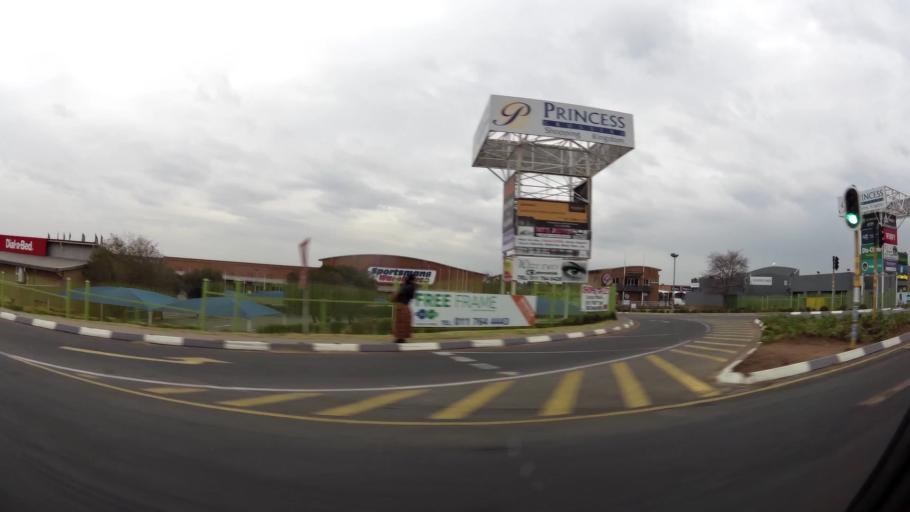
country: ZA
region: Gauteng
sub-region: City of Johannesburg Metropolitan Municipality
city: Roodepoort
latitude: -26.1298
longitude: 27.8513
